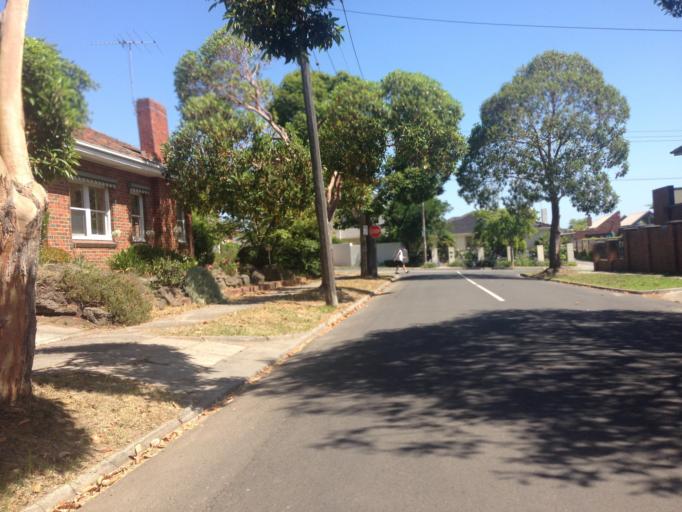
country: AU
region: Victoria
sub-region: Boroondara
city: Kew East
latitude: -37.7949
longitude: 145.0728
